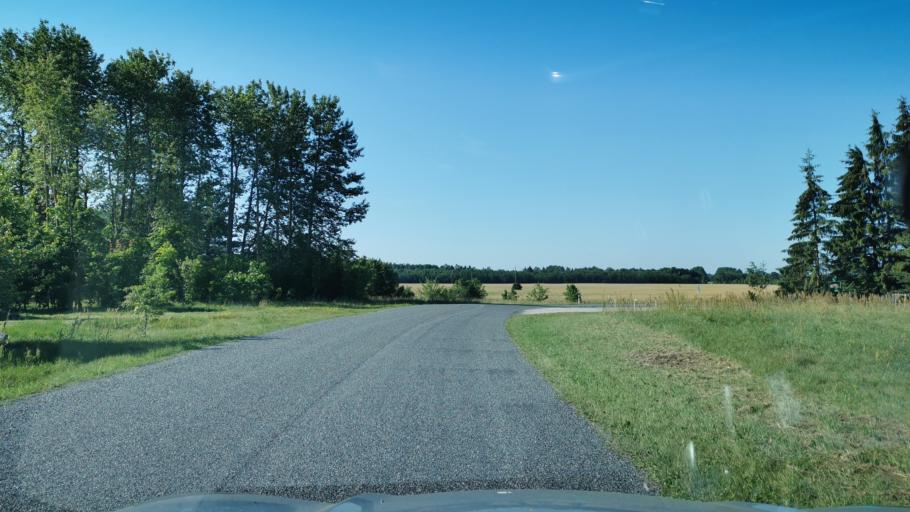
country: EE
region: Harju
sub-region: Paldiski linn
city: Paldiski
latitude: 59.2173
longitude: 24.0465
